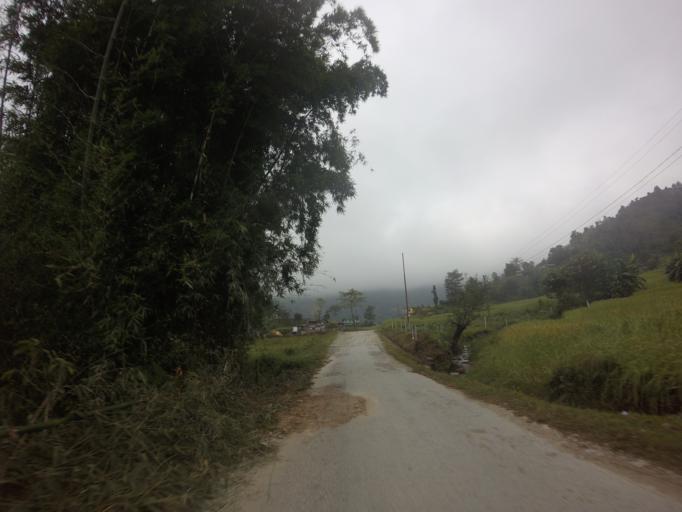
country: NP
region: Western Region
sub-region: Gandaki Zone
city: Pokhara
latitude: 28.2323
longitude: 83.9312
